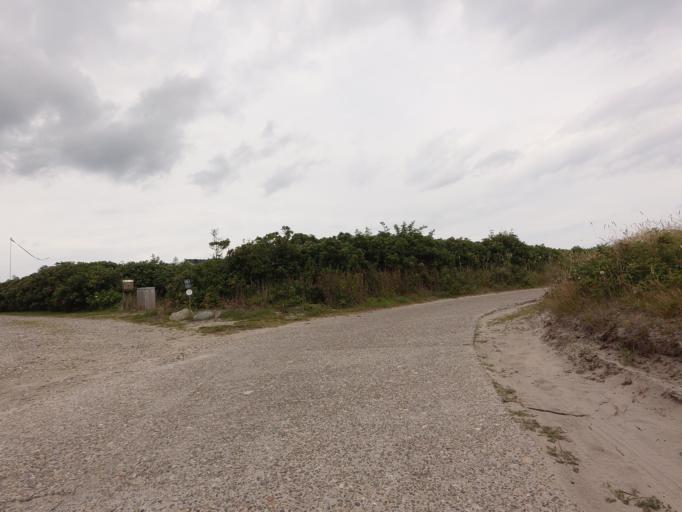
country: DK
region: North Denmark
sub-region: Jammerbugt Kommune
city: Pandrup
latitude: 57.3098
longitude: 9.6521
